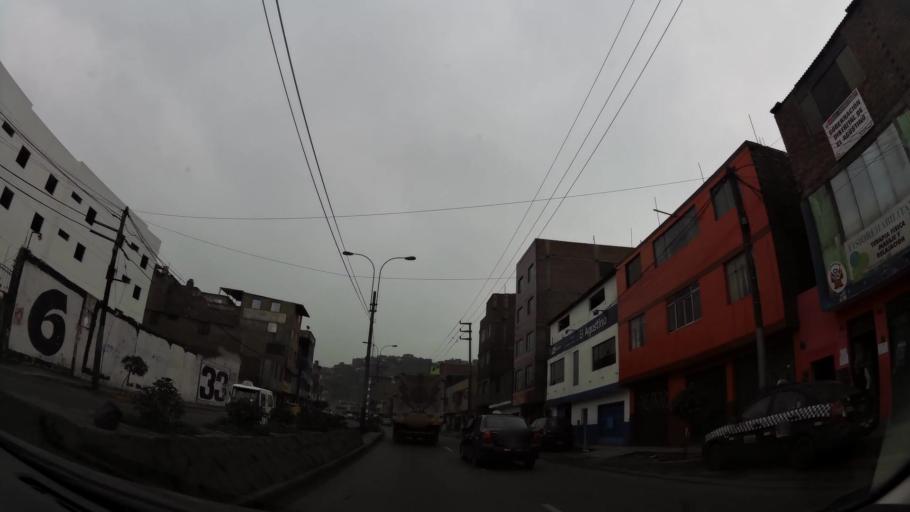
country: PE
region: Lima
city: Lima
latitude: -12.0447
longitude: -76.9982
